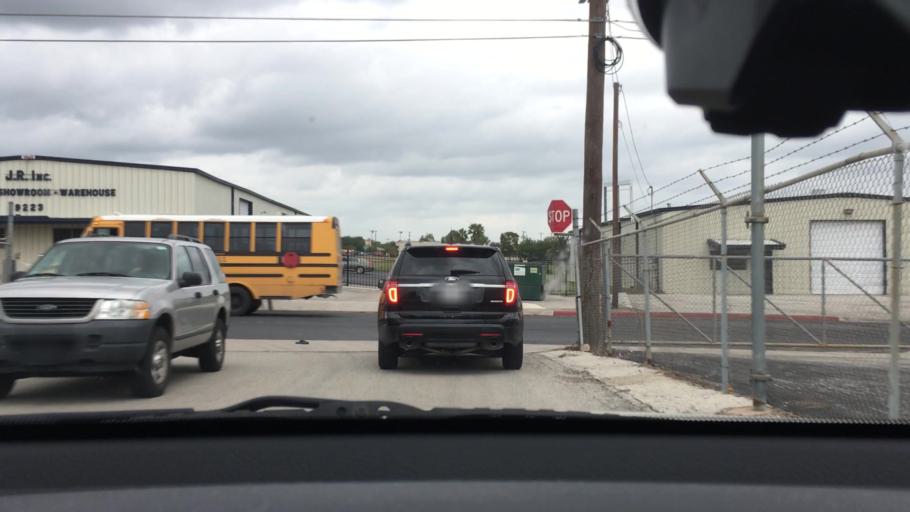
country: US
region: Texas
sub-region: Bexar County
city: Converse
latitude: 29.5125
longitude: -98.3056
